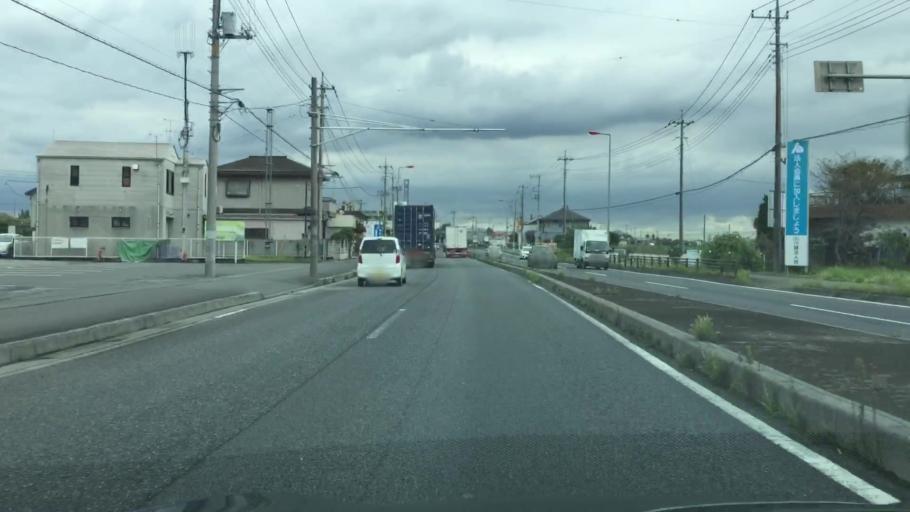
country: JP
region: Saitama
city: Kawagoe
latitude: 35.9162
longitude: 139.5220
